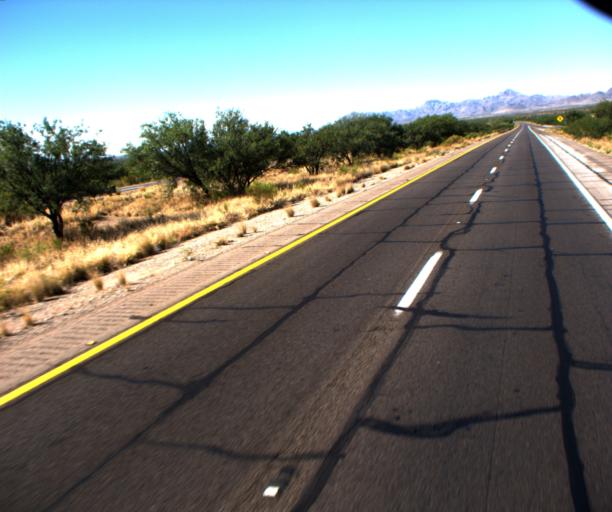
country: US
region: Arizona
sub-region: Pima County
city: Arivaca Junction
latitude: 31.7254
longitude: -111.0588
